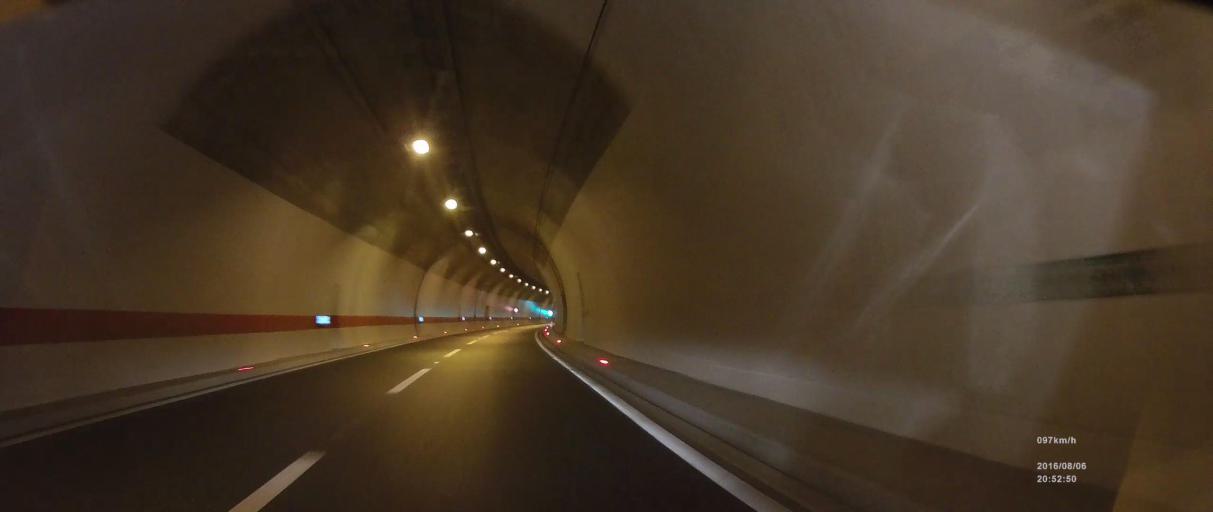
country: BA
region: Federation of Bosnia and Herzegovina
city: Ljubuski
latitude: 43.1367
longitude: 17.4829
